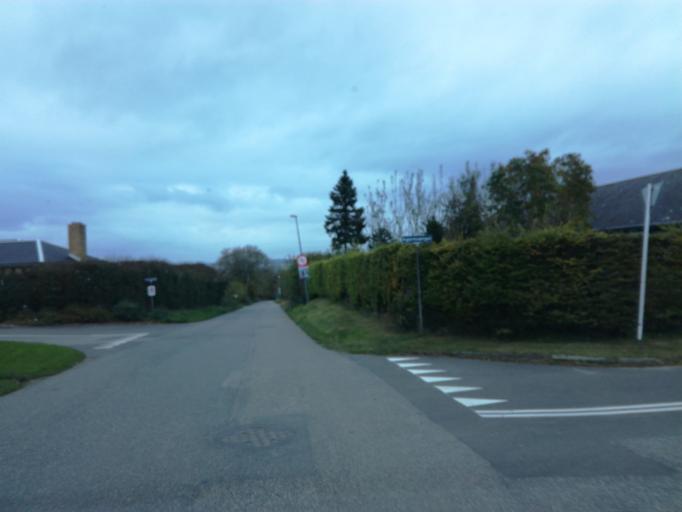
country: DK
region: South Denmark
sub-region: Fredericia Kommune
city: Fredericia
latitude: 55.6180
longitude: 9.7911
